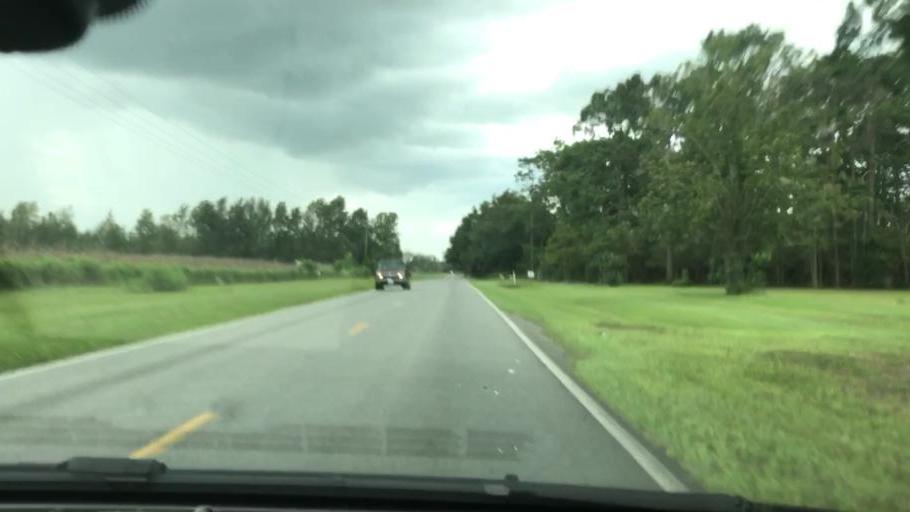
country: US
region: Florida
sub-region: Madison County
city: Madison
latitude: 30.3954
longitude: -83.3004
